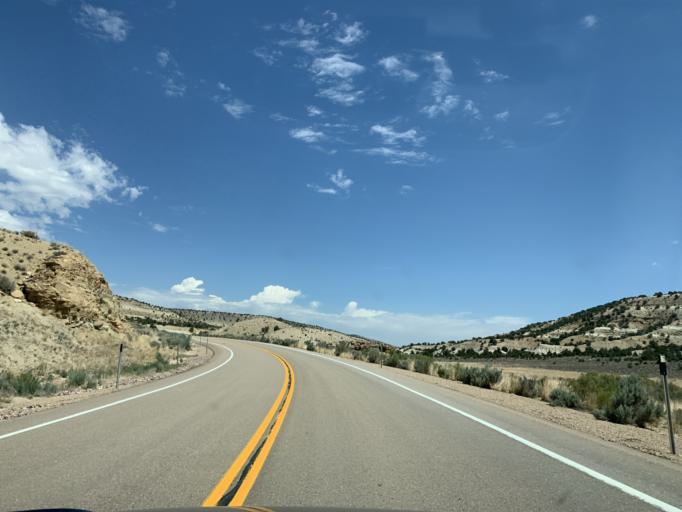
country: US
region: Utah
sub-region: Duchesne County
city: Duchesne
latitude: 39.9542
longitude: -110.1914
